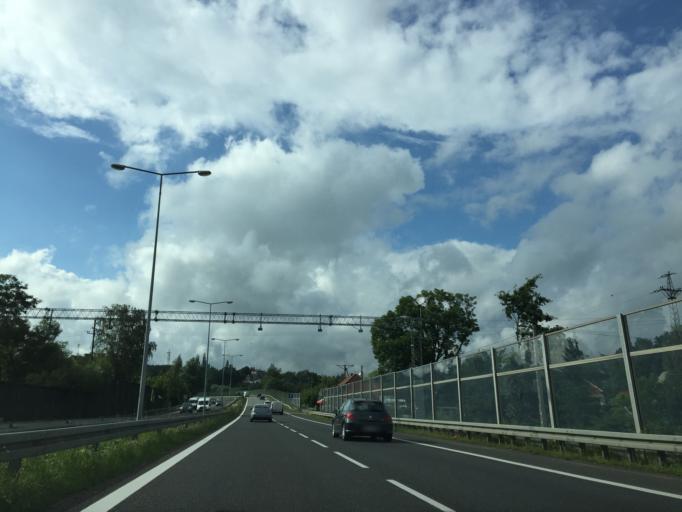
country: PL
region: Lesser Poland Voivodeship
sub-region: Powiat myslenicki
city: Myslenice
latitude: 49.8384
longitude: 19.9478
